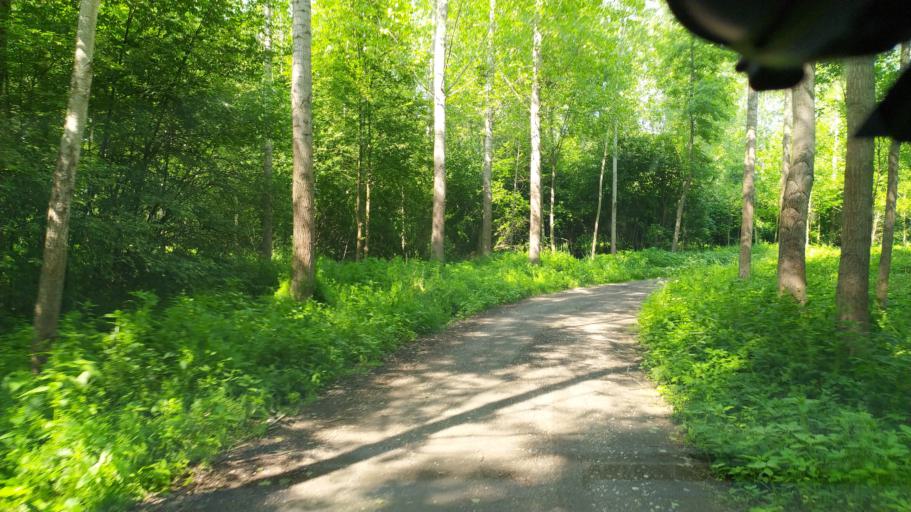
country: AT
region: Lower Austria
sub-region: Politischer Bezirk Amstetten
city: Strengberg
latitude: 48.1736
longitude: 14.6876
